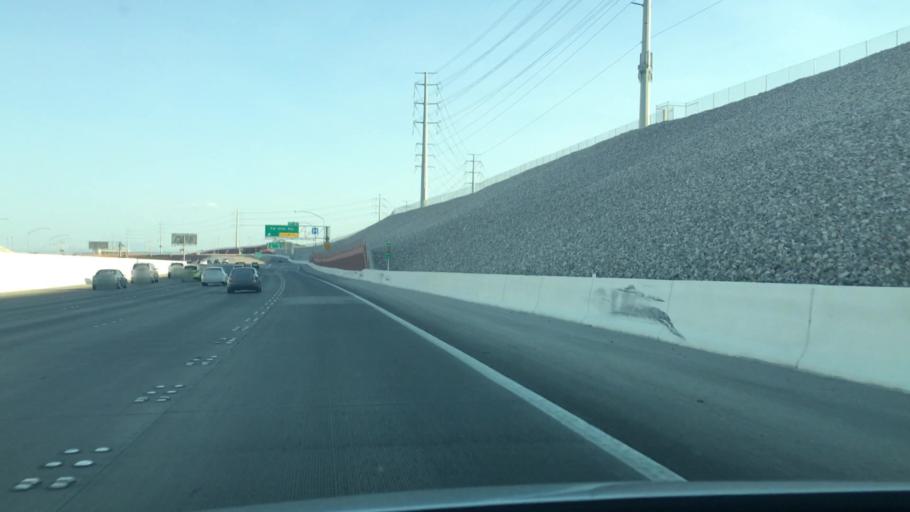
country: US
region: Nevada
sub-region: Clark County
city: Summerlin South
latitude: 36.1859
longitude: -115.3439
